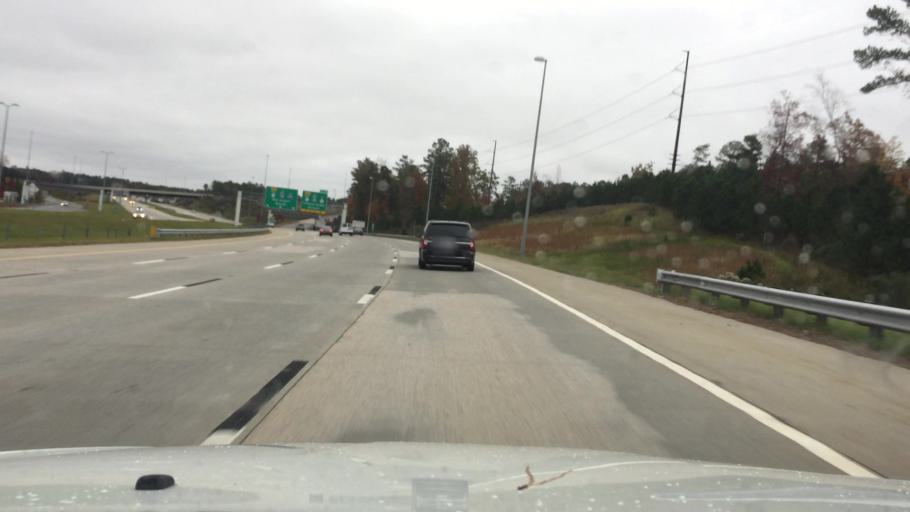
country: US
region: North Carolina
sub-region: Wake County
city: Morrisville
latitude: 35.8477
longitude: -78.8674
